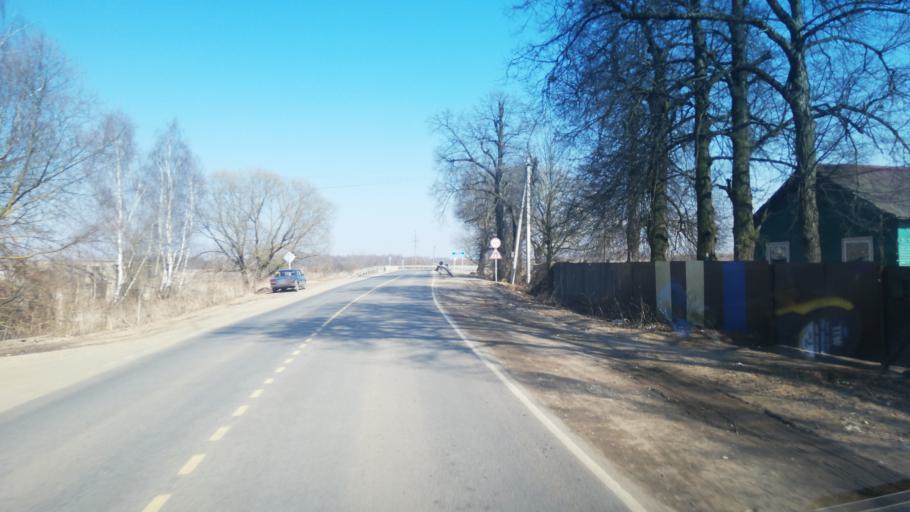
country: RU
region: Jaroslavl
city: Semibratovo
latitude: 57.2333
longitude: 39.5028
